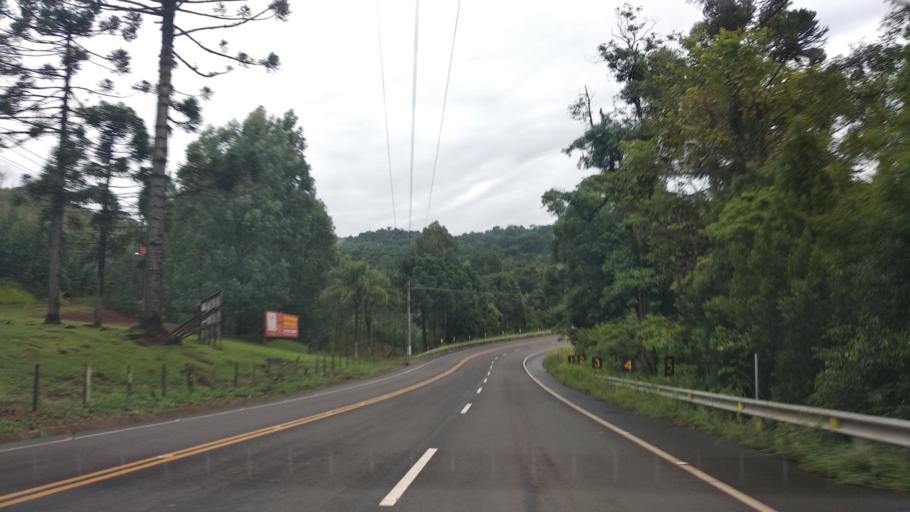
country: BR
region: Santa Catarina
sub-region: Videira
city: Videira
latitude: -27.0518
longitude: -51.1718
